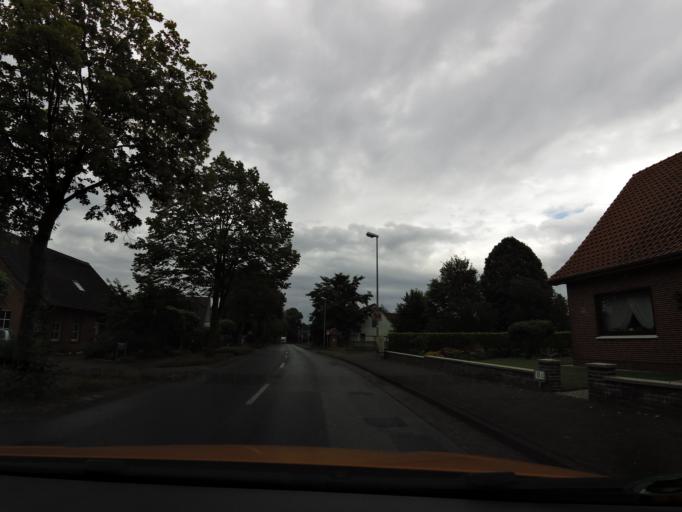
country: DE
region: Lower Saxony
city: Bassum
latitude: 52.8449
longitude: 8.7072
